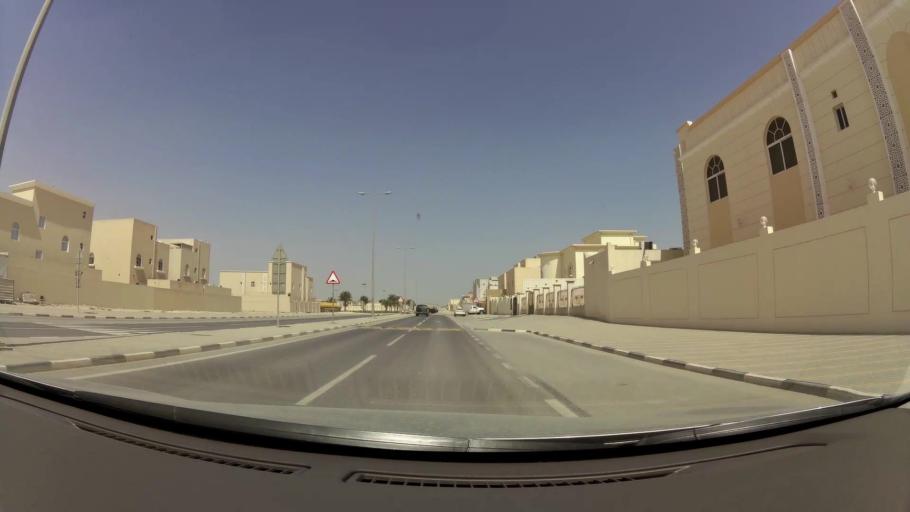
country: QA
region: Baladiyat Umm Salal
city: Umm Salal Muhammad
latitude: 25.3766
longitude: 51.4618
